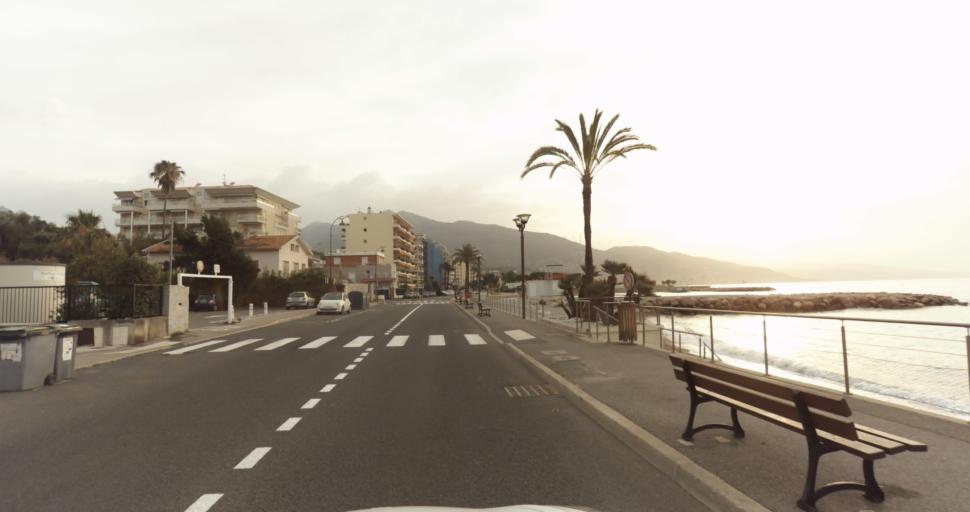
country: FR
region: Provence-Alpes-Cote d'Azur
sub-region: Departement des Alpes-Maritimes
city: Roquebrune-Cap-Martin
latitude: 43.7615
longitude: 7.4843
